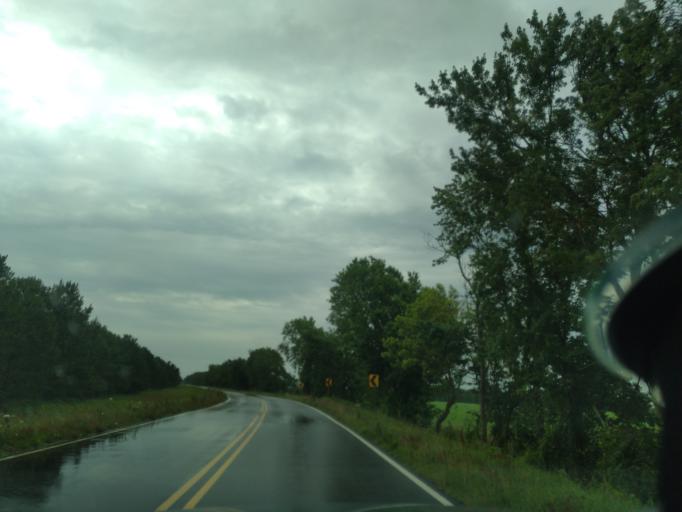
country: US
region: North Carolina
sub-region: Washington County
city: Plymouth
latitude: 35.8446
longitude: -76.5545
